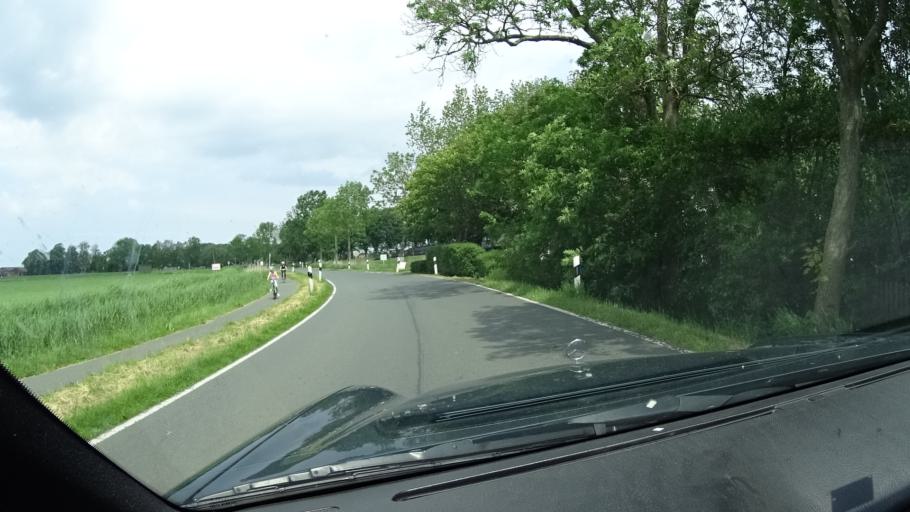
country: DE
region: Lower Saxony
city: Butjadingen
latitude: 53.5815
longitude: 8.2696
